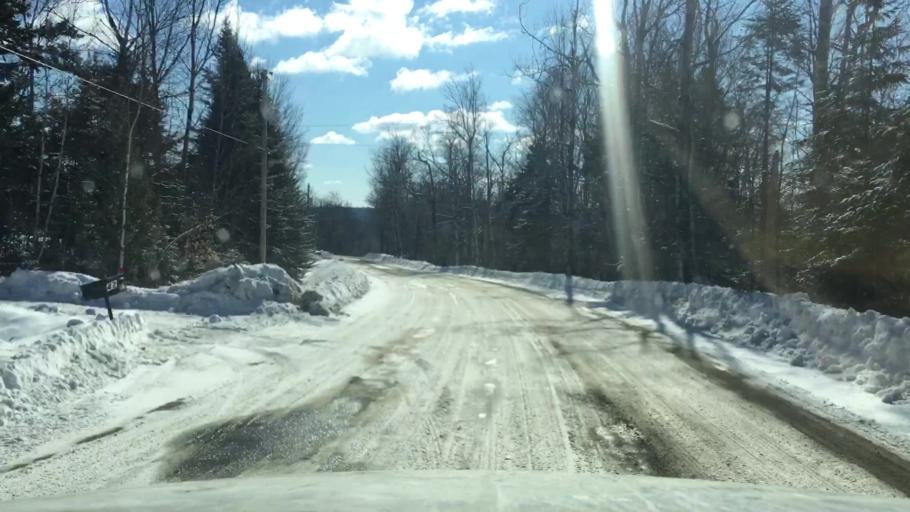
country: US
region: Maine
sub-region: Washington County
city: Calais
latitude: 45.0781
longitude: -67.5057
